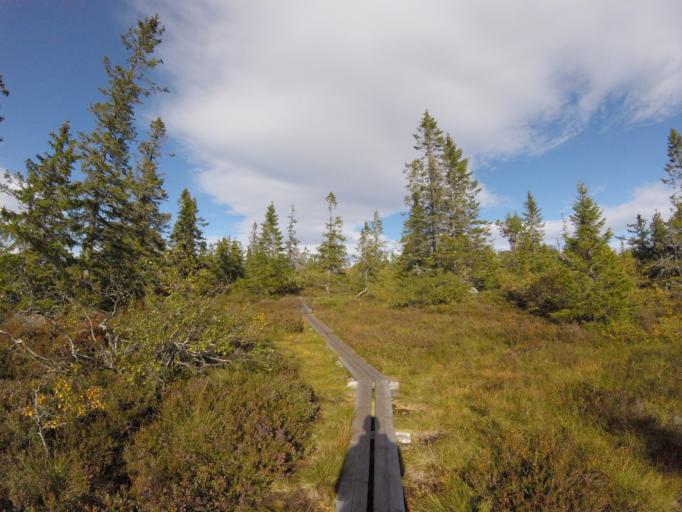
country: NO
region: Buskerud
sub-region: Flesberg
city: Lampeland
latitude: 59.7662
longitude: 9.4121
